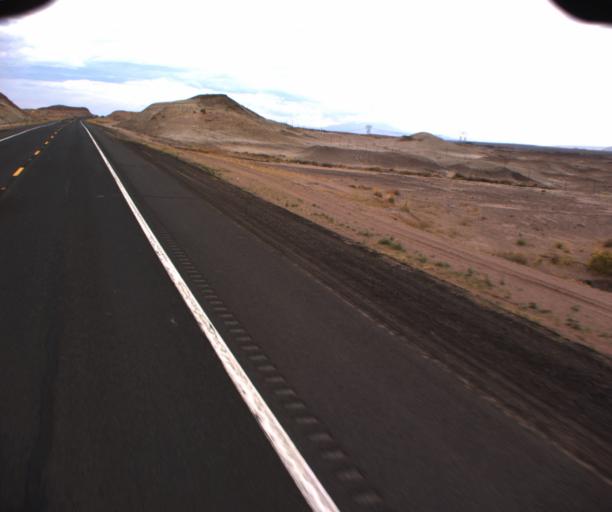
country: US
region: Arizona
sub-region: Coconino County
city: Tuba City
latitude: 36.0045
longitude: -111.3940
